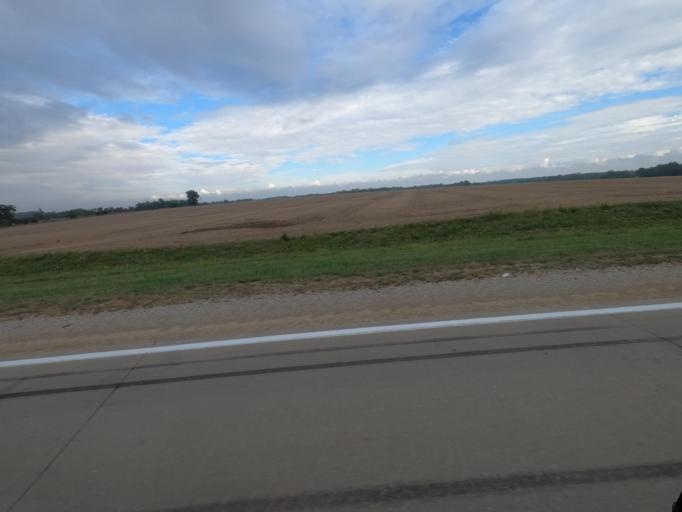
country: US
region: Iowa
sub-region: Henry County
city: Mount Pleasant
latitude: 40.8112
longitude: -91.7035
